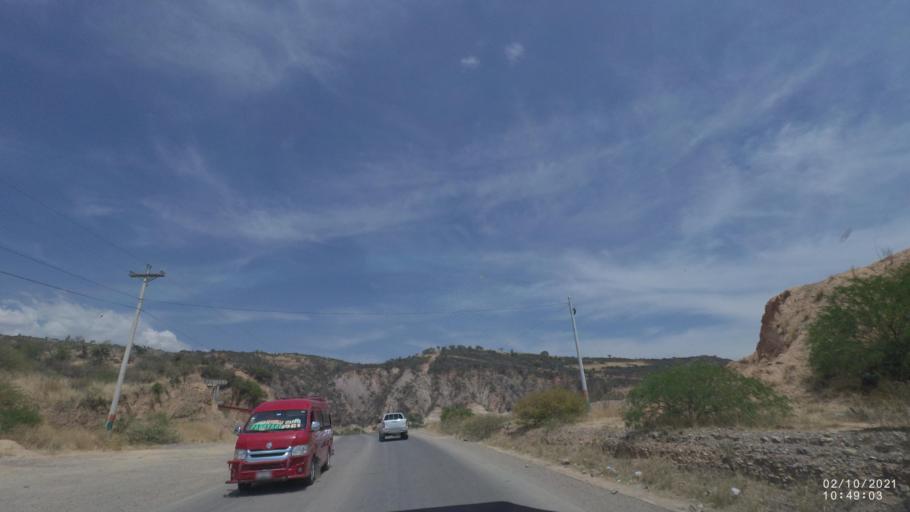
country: BO
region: Cochabamba
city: Sipe Sipe
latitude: -17.5803
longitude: -66.3411
